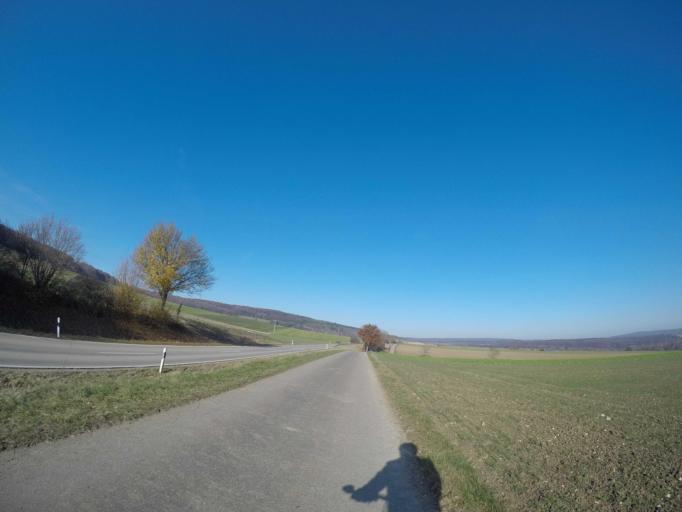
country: DE
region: Baden-Wuerttemberg
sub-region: Tuebingen Region
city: Emeringen
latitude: 48.2262
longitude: 9.5209
